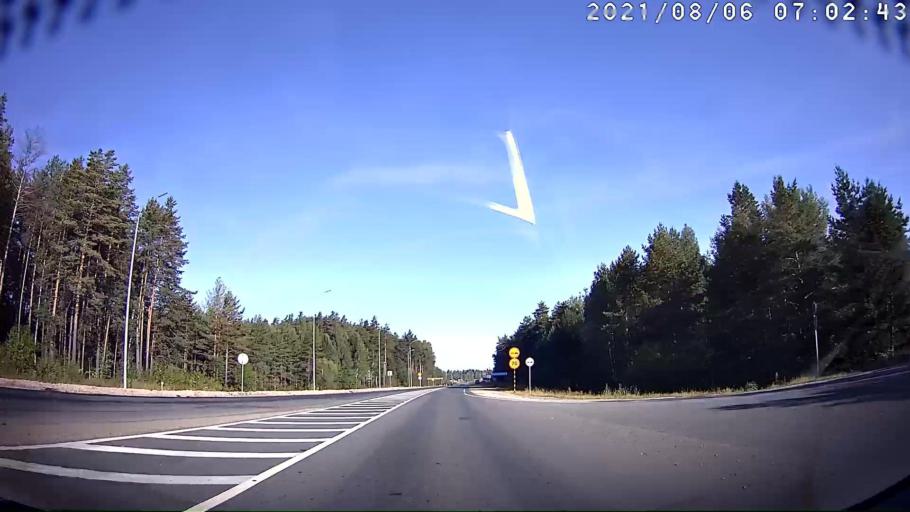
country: RU
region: Mariy-El
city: Yoshkar-Ola
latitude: 56.5365
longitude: 47.9914
